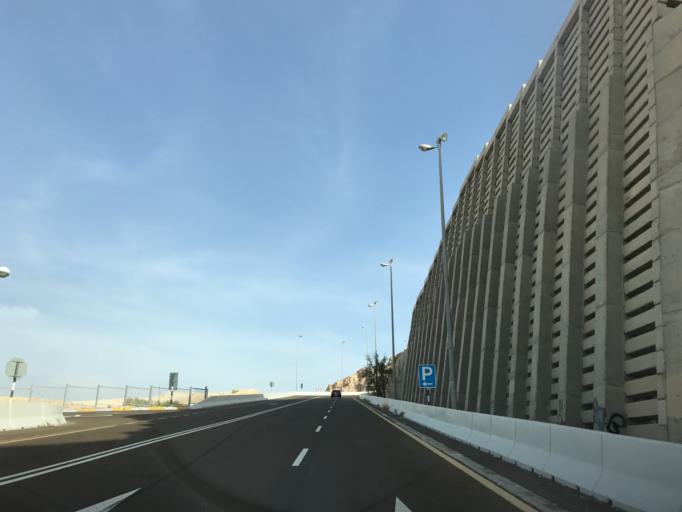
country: AE
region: Abu Dhabi
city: Al Ain
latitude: 24.0806
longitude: 55.7704
